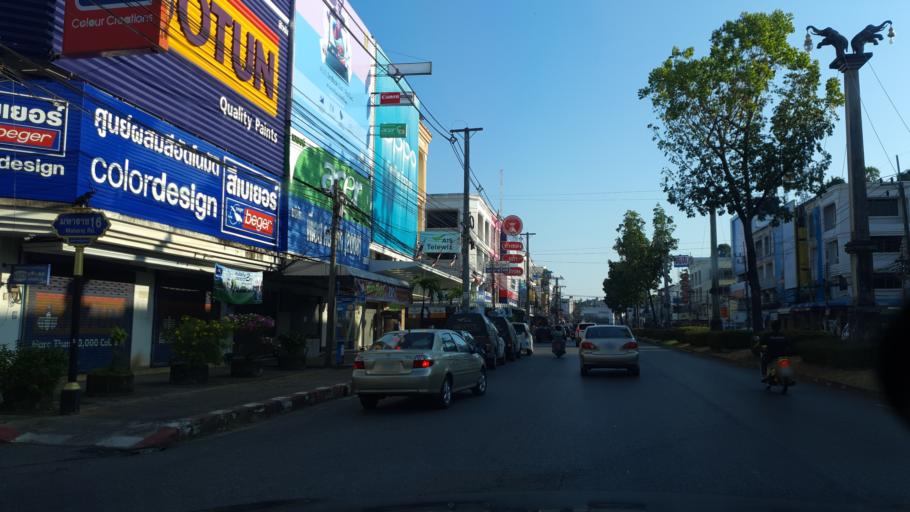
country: TH
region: Krabi
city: Krabi
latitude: 8.0665
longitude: 98.9150
